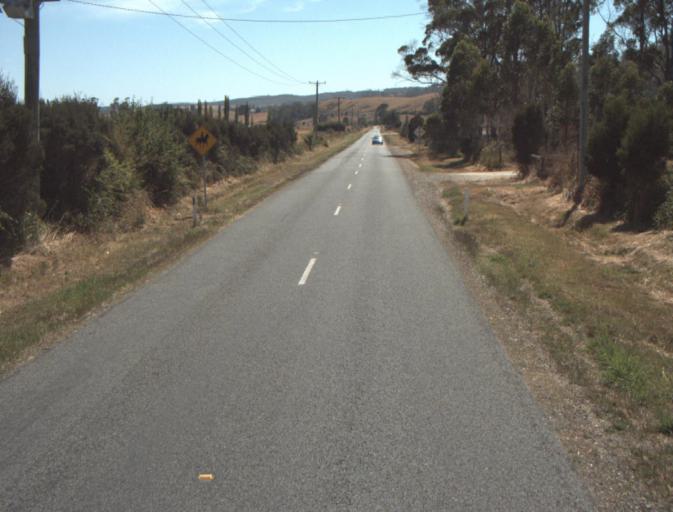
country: AU
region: Tasmania
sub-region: Launceston
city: Mayfield
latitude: -41.2557
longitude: 147.1466
